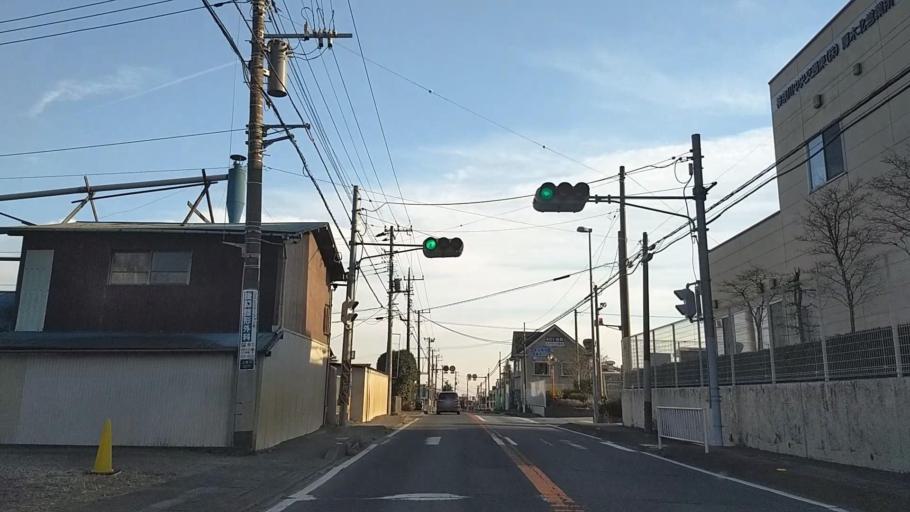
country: JP
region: Kanagawa
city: Zama
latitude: 35.5134
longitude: 139.3001
